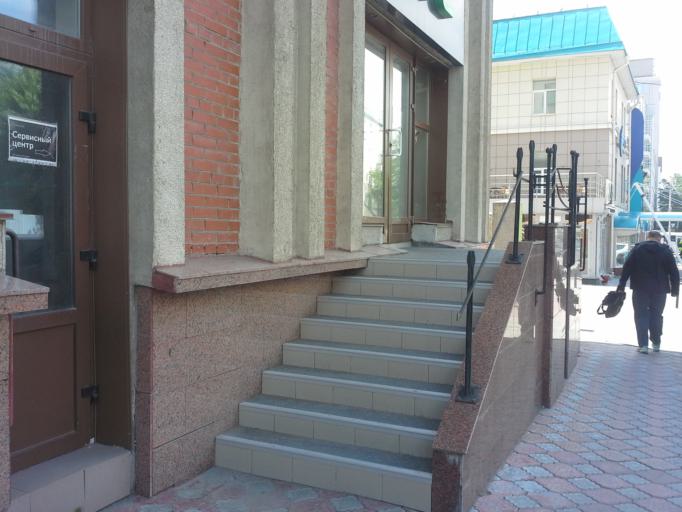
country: RU
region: Novosibirsk
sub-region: Novosibirskiy Rayon
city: Novosibirsk
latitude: 55.0237
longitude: 82.9240
